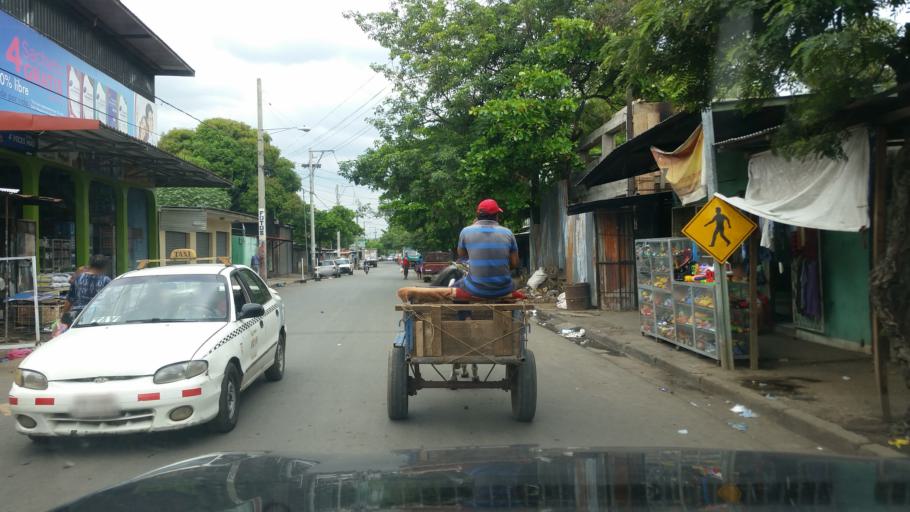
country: NI
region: Managua
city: Managua
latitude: 12.1455
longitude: -86.2634
